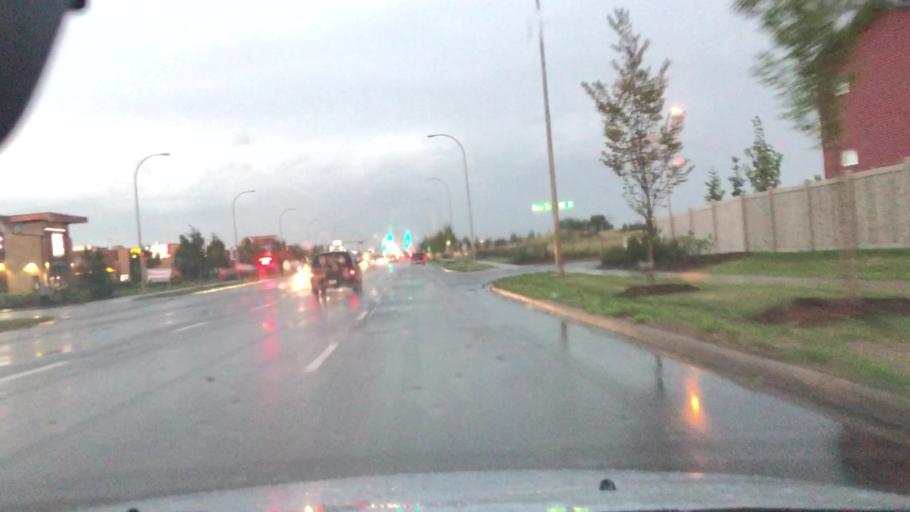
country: CA
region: Alberta
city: St. Albert
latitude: 53.6287
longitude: -113.5481
